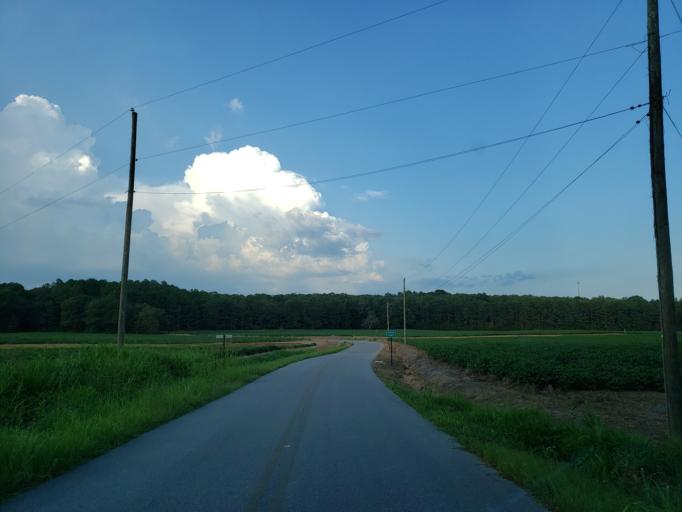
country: US
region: Georgia
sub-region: Bartow County
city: Euharlee
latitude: 34.0826
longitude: -84.9388
